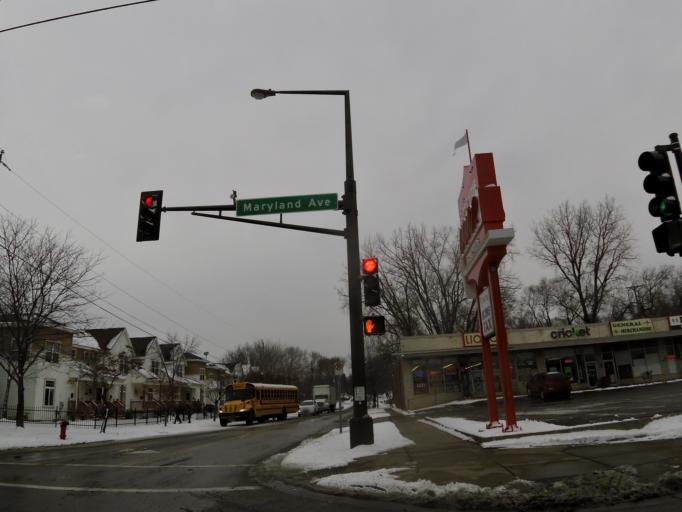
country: US
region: Minnesota
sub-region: Ramsey County
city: Maplewood
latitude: 44.9776
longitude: -93.0430
